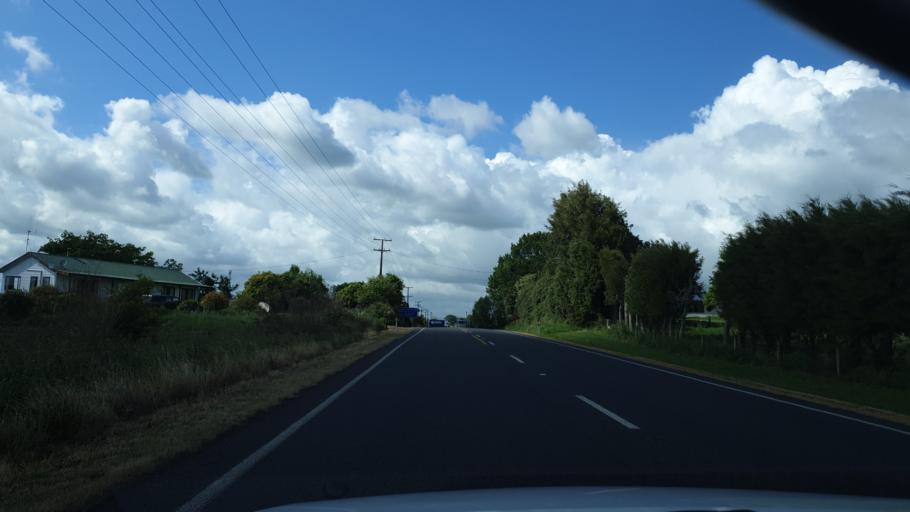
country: NZ
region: Waikato
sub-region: Hauraki District
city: Paeroa
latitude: -37.5118
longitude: 175.4965
